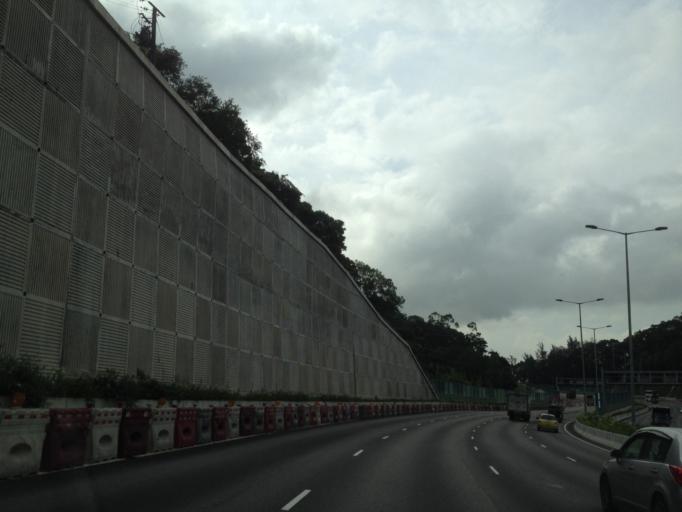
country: HK
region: Tai Po
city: Tai Po
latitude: 22.4412
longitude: 114.1590
